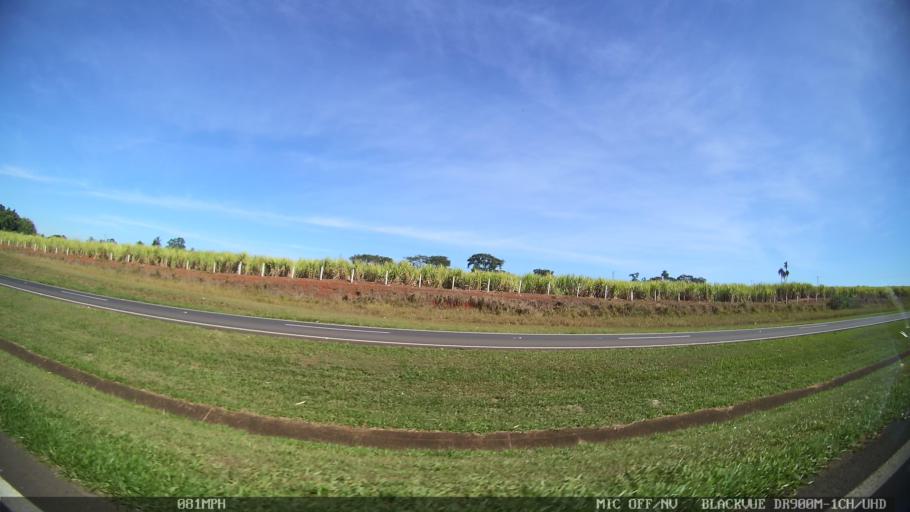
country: BR
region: Sao Paulo
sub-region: Leme
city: Leme
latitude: -22.1130
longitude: -47.4120
